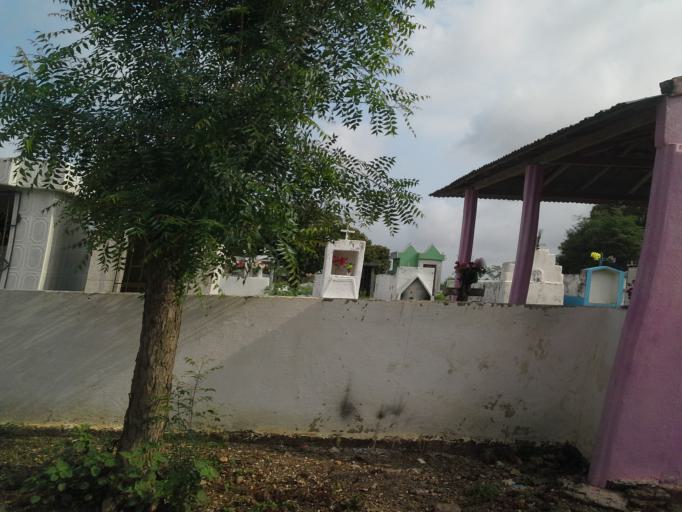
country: CO
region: Cordoba
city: Chima
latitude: 9.1030
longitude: -75.6242
